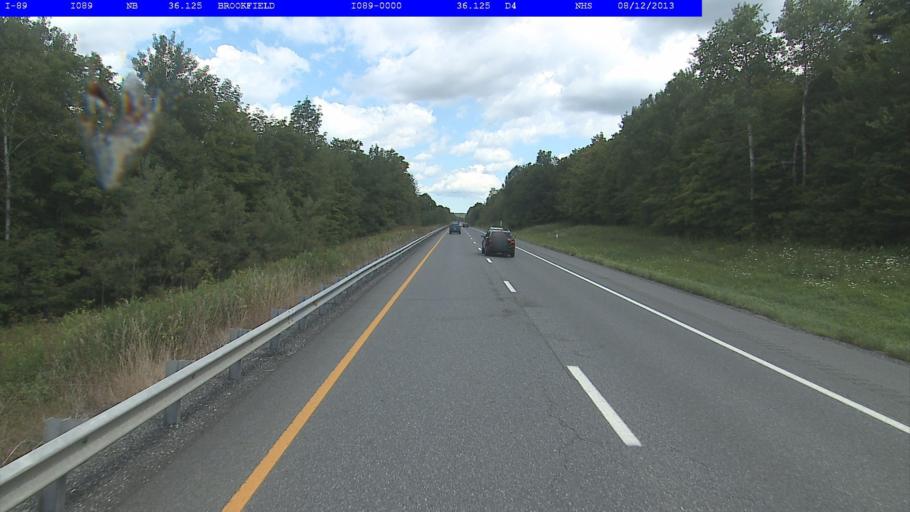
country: US
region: Vermont
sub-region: Orange County
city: Randolph
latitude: 44.0192
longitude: -72.6169
